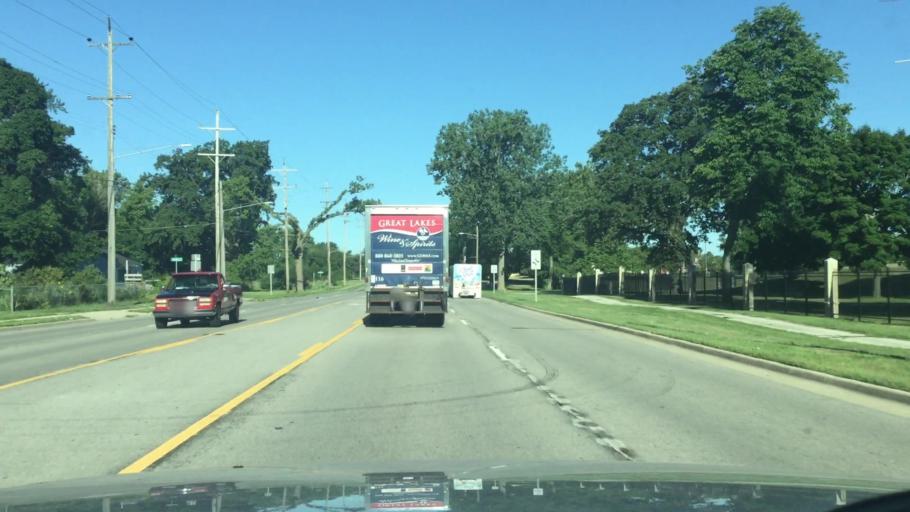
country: US
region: Michigan
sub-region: Saginaw County
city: Saginaw
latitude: 43.4101
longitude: -83.9576
